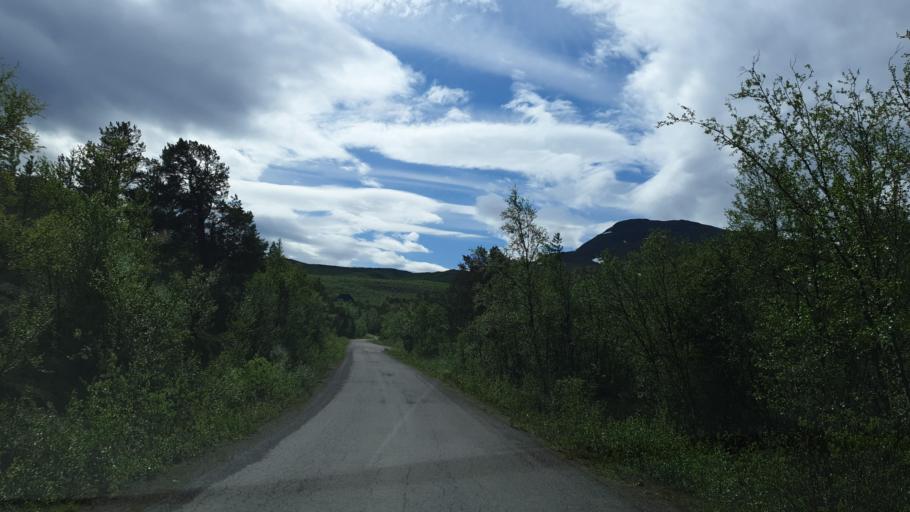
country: SE
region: Norrbotten
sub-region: Kiruna Kommun
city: Kiruna
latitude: 68.2247
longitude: 19.7168
